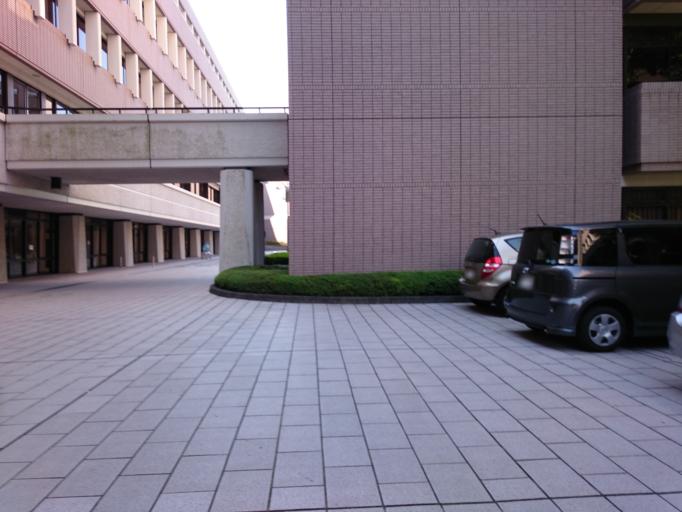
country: JP
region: Tokyo
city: Hachioji
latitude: 35.6251
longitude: 139.3437
